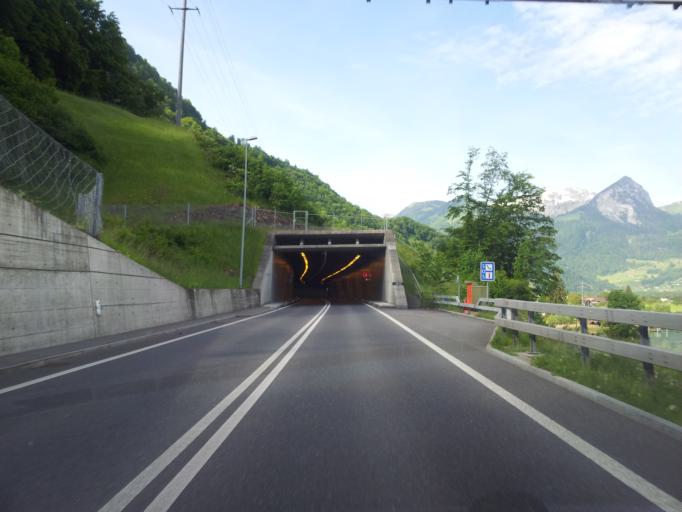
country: CH
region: Obwalden
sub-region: Obwalden
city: Giswil
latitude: 46.8470
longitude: 8.2064
